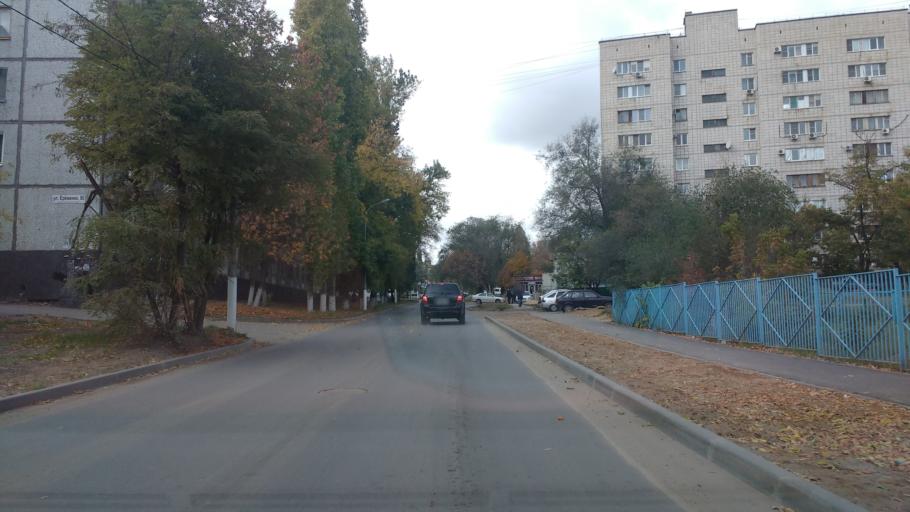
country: RU
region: Volgograd
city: Vodstroy
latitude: 48.7728
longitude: 44.5515
